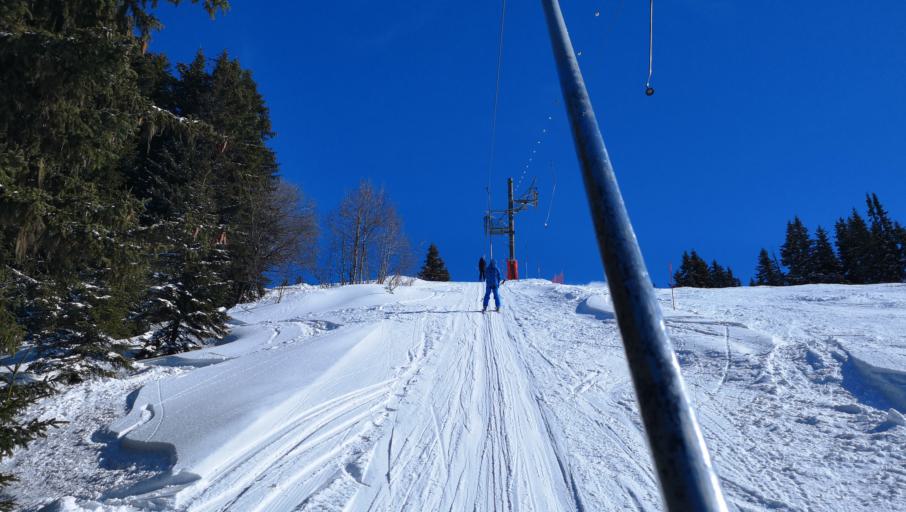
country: FR
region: Rhone-Alpes
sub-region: Departement de la Haute-Savoie
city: Megeve
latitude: 45.8407
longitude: 6.6624
